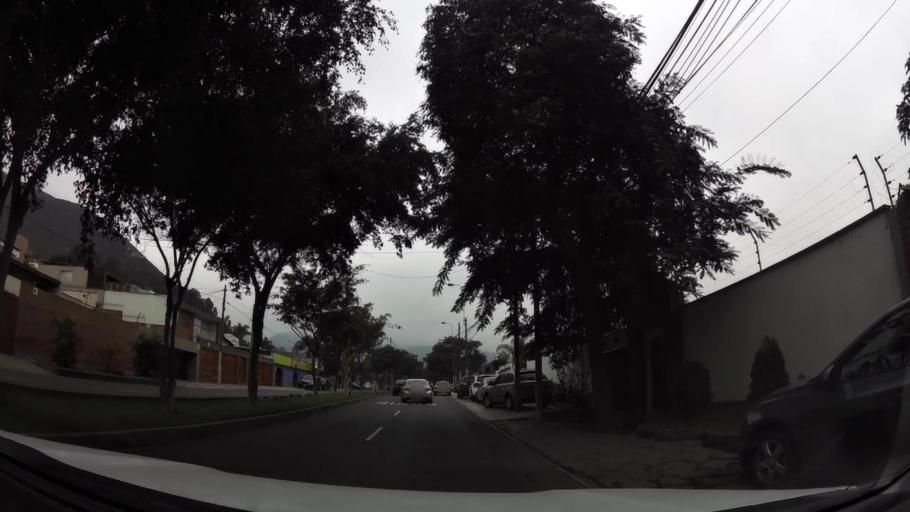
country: PE
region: Lima
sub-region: Lima
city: La Molina
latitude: -12.0797
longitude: -76.9221
